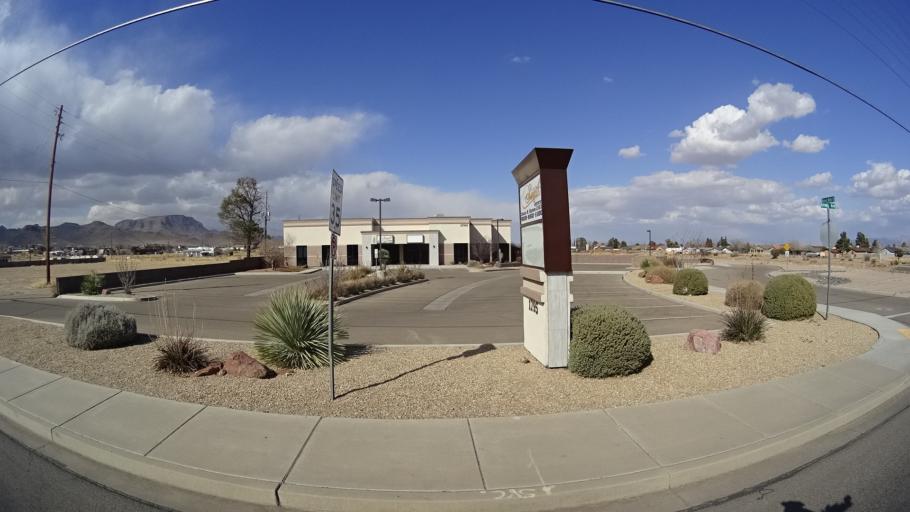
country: US
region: Arizona
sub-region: Mohave County
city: New Kingman-Butler
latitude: 35.2249
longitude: -114.0316
